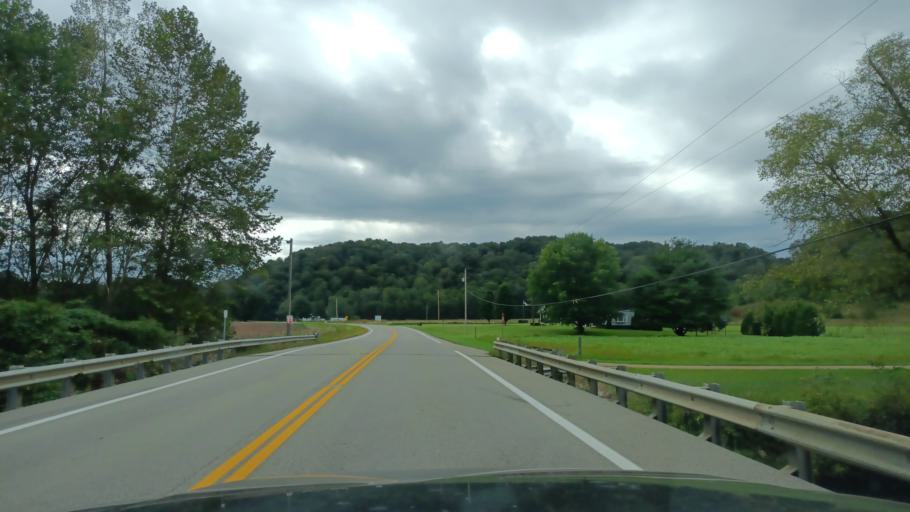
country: US
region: Ohio
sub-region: Vinton County
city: McArthur
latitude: 39.2746
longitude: -82.6295
